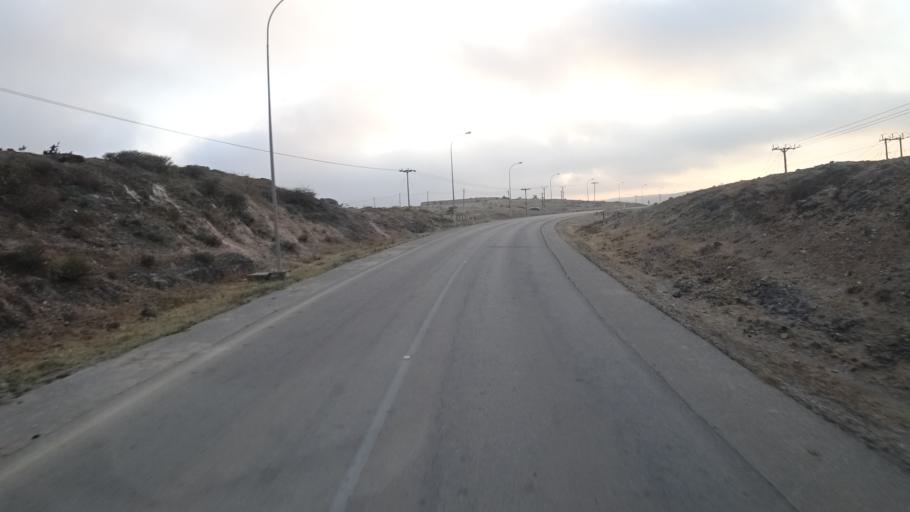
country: OM
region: Zufar
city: Salalah
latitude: 17.1270
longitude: 53.9539
